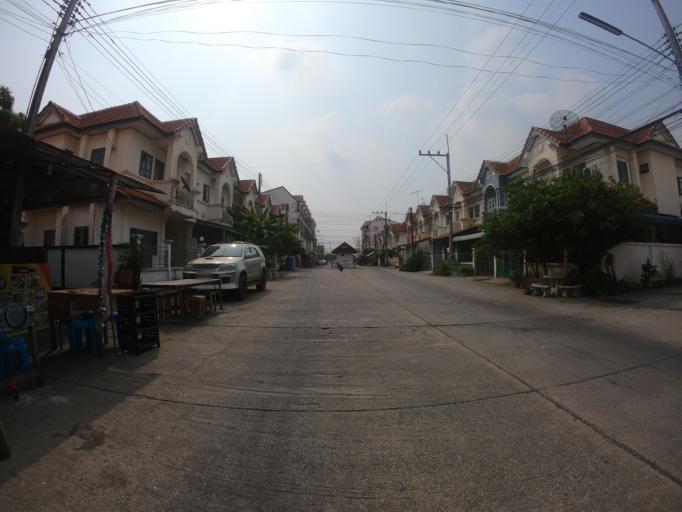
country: TH
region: Pathum Thani
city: Nong Suea
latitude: 14.0661
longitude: 100.8587
